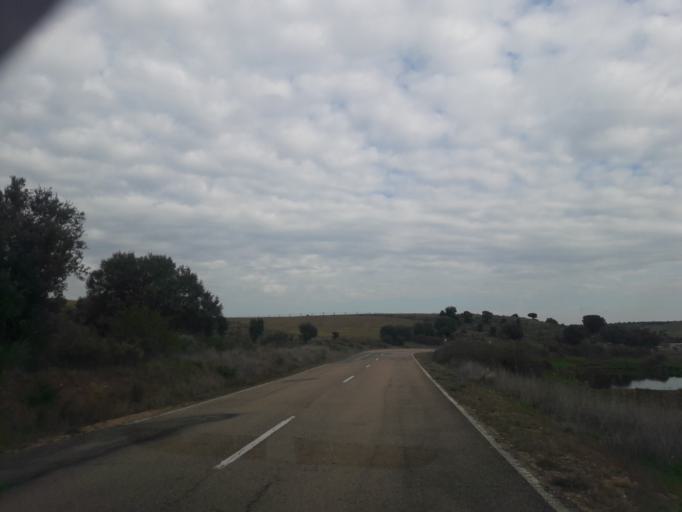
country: ES
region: Castille and Leon
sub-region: Provincia de Salamanca
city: Pastores
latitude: 40.5404
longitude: -6.5276
